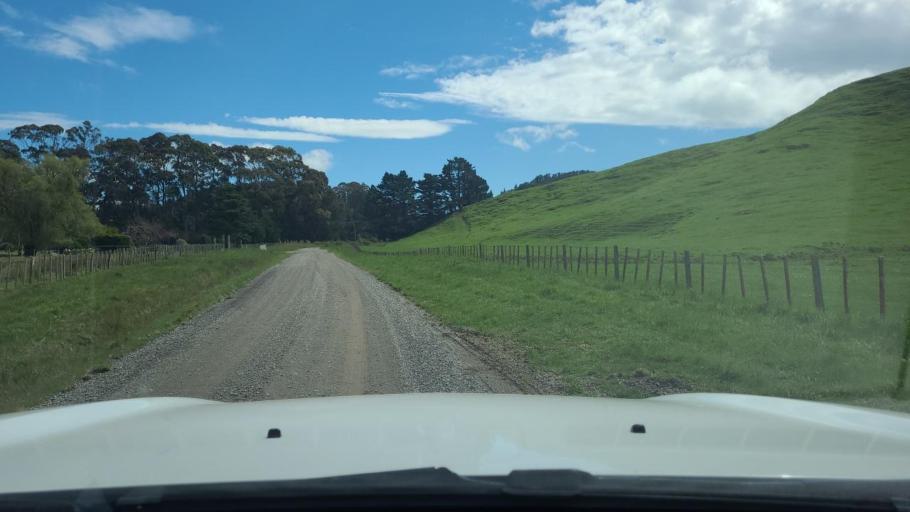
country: NZ
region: Wellington
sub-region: South Wairarapa District
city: Waipawa
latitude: -41.3215
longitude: 175.3800
